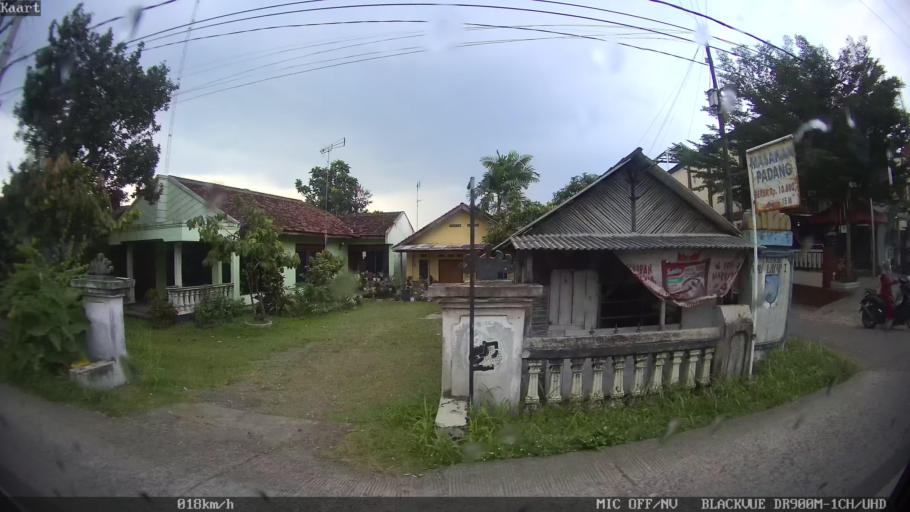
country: ID
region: Lampung
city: Gedongtataan
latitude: -5.3767
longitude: 105.1277
